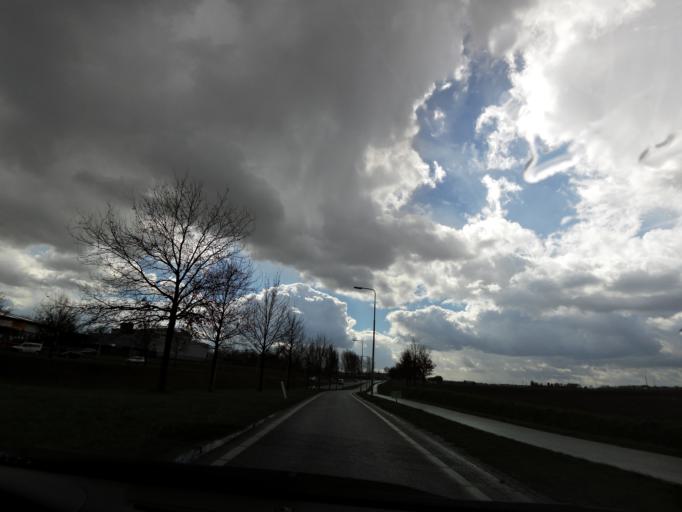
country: NL
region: Limburg
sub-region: Gemeente Sittard-Geleen
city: Limbricht
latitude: 51.0078
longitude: 5.8448
